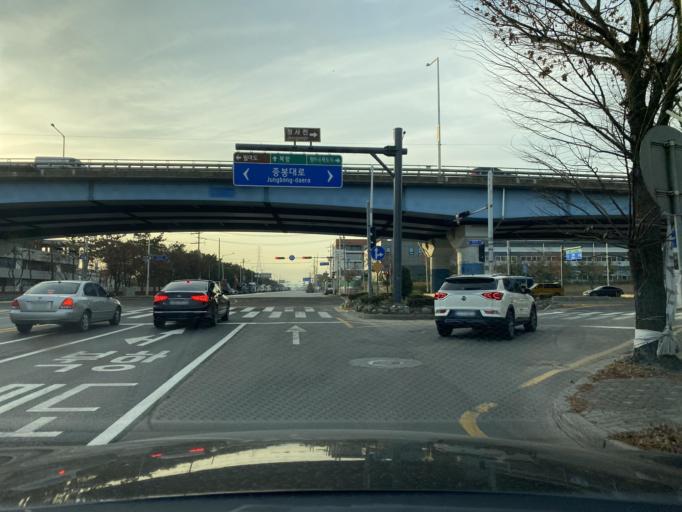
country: KR
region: Incheon
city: Incheon
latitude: 37.4993
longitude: 126.6485
